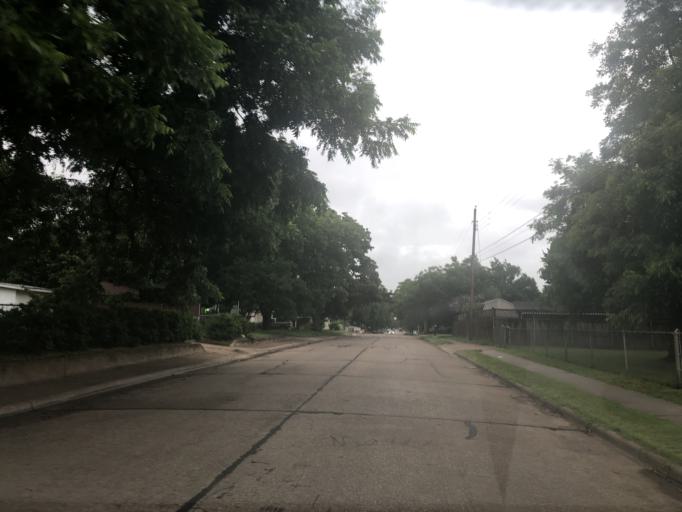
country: US
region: Texas
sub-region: Dallas County
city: Irving
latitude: 32.7975
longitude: -96.9516
